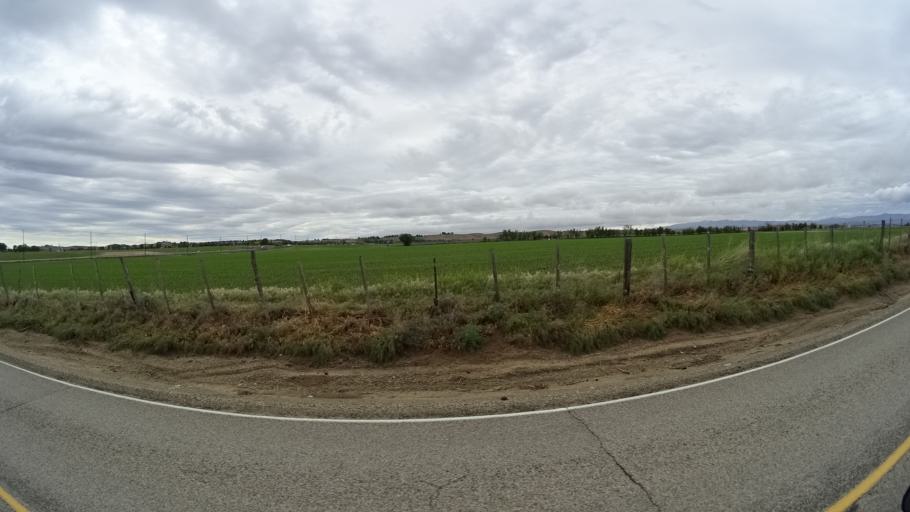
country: US
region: Idaho
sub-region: Ada County
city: Star
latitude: 43.7097
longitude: -116.4519
